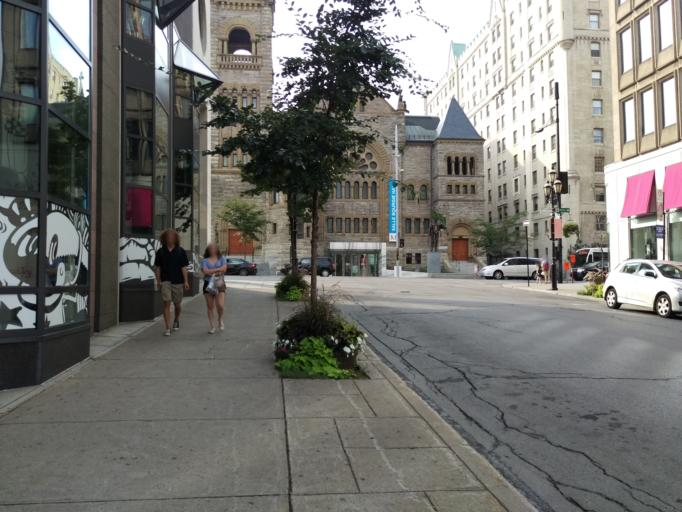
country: CA
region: Quebec
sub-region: Montreal
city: Montreal
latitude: 45.4988
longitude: -73.5789
